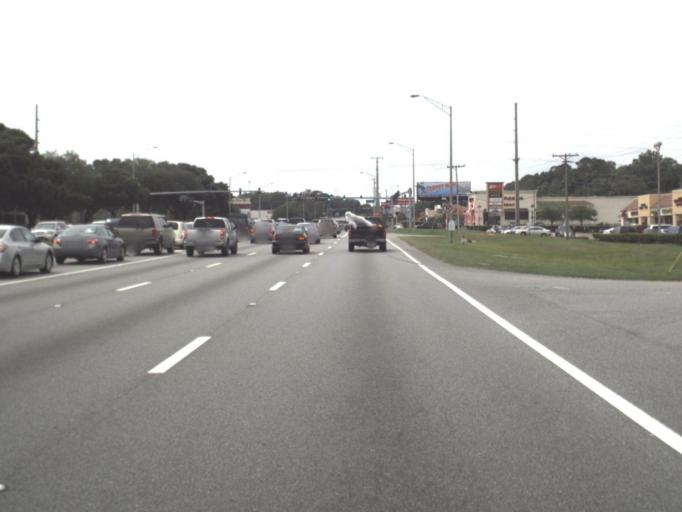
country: US
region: Florida
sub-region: Clay County
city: Bellair-Meadowbrook Terrace
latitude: 30.1887
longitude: -81.7395
